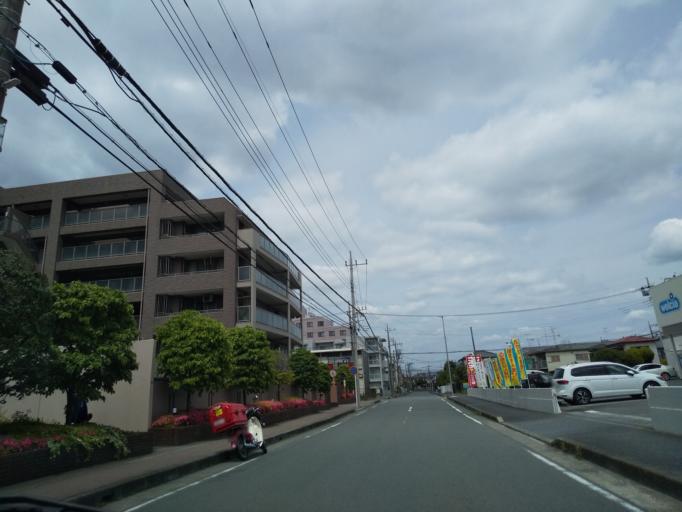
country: JP
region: Kanagawa
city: Zama
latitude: 35.5714
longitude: 139.3622
